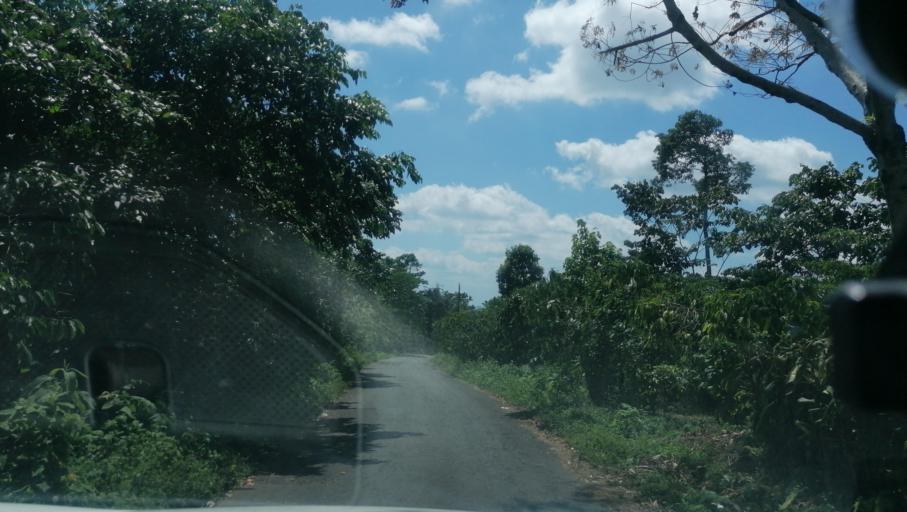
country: MX
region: Chiapas
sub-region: Cacahoatan
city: Benito Juarez
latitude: 15.0602
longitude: -92.1459
